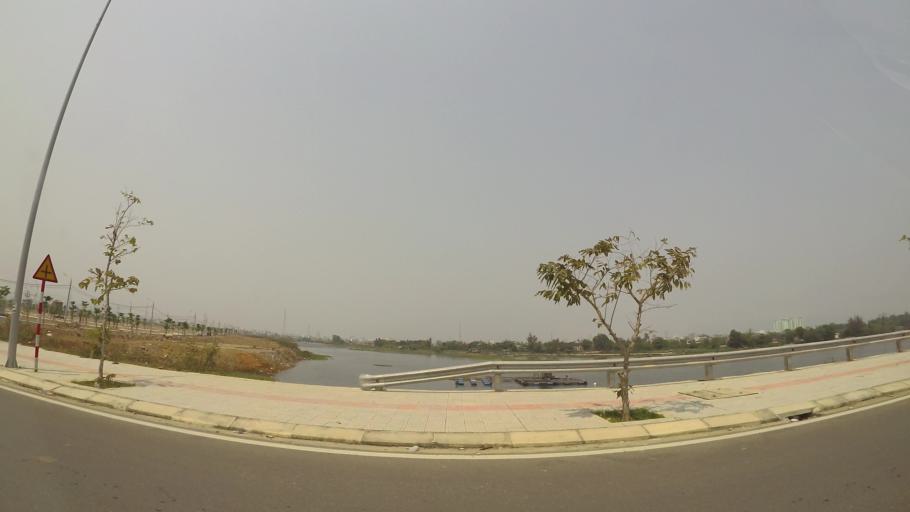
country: VN
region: Da Nang
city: Ngu Hanh Son
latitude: 16.0119
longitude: 108.2458
